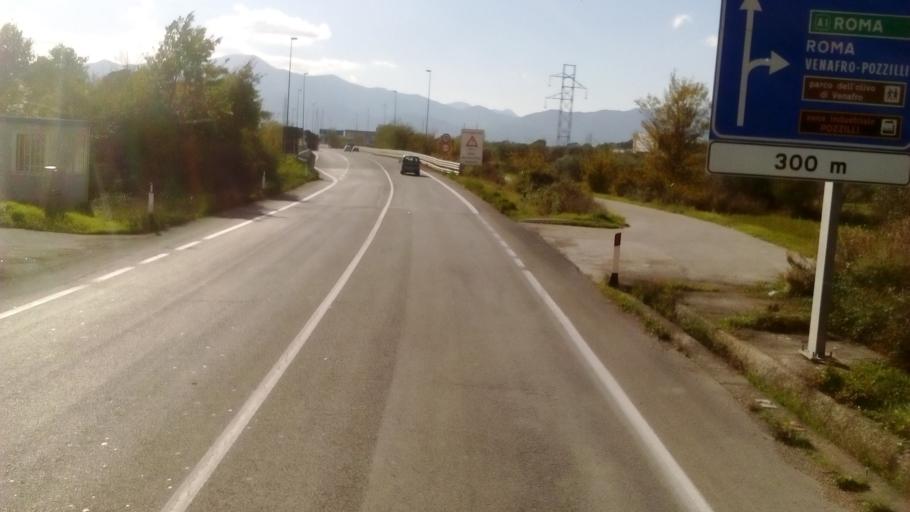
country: IT
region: Molise
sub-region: Provincia di Isernia
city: Taverna Ravindola
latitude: 41.5120
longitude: 14.1165
